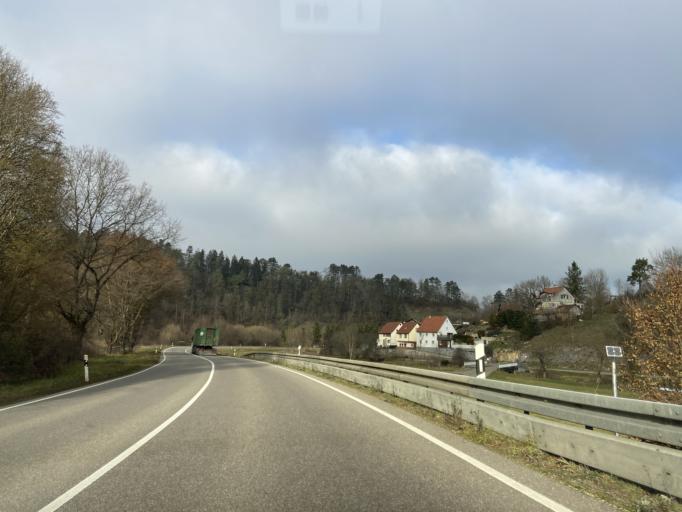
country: DE
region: Baden-Wuerttemberg
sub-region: Tuebingen Region
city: Veringenstadt
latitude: 48.1757
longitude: 9.2086
